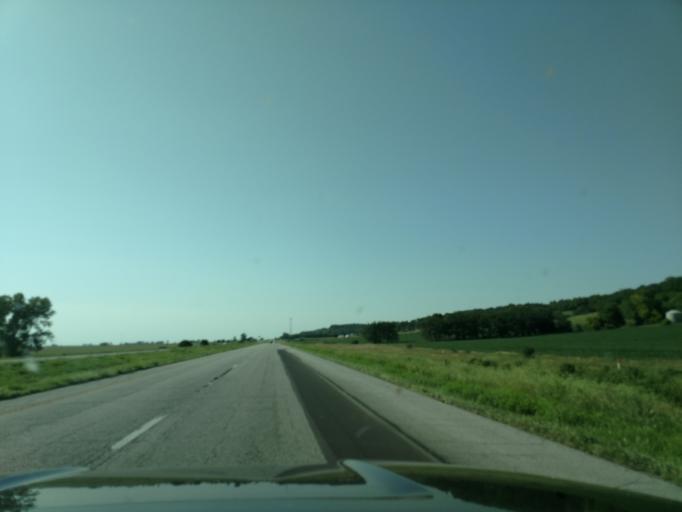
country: US
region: Missouri
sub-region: Atchison County
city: Rock Port
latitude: 40.3767
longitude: -95.5385
